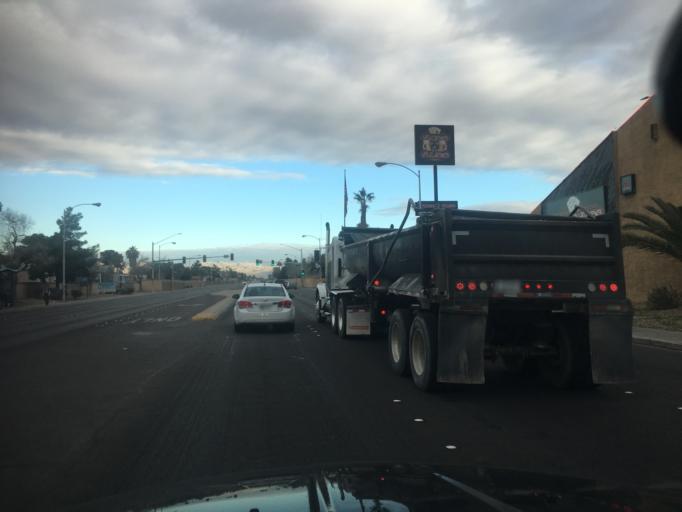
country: US
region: Nevada
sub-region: Clark County
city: Whitney
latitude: 36.1212
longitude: -115.0650
